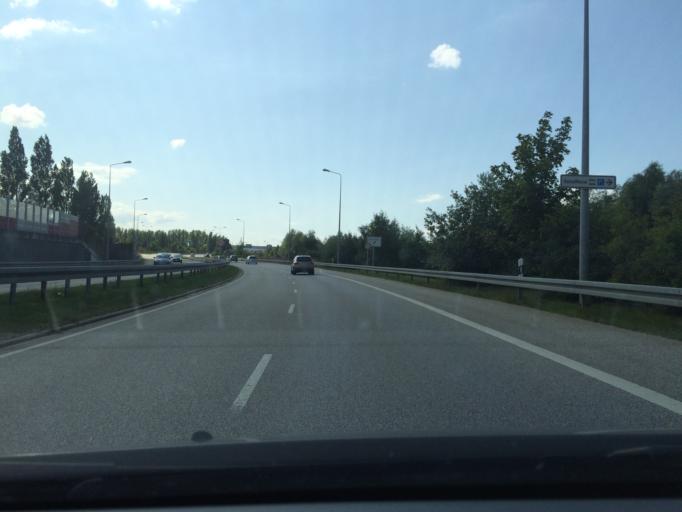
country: DE
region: Mecklenburg-Vorpommern
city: Warnemuende
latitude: 54.1385
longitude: 12.0718
